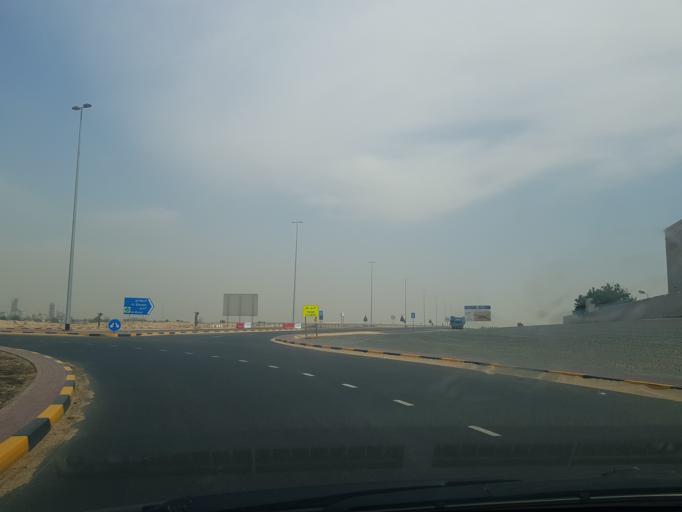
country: AE
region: Ash Shariqah
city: Sharjah
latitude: 25.2858
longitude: 55.5909
